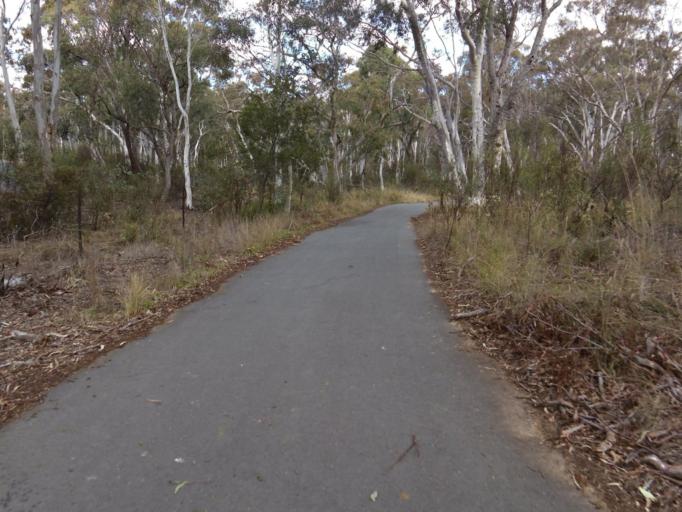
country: AU
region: Australian Capital Territory
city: Macquarie
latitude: -35.2508
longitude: 149.0936
